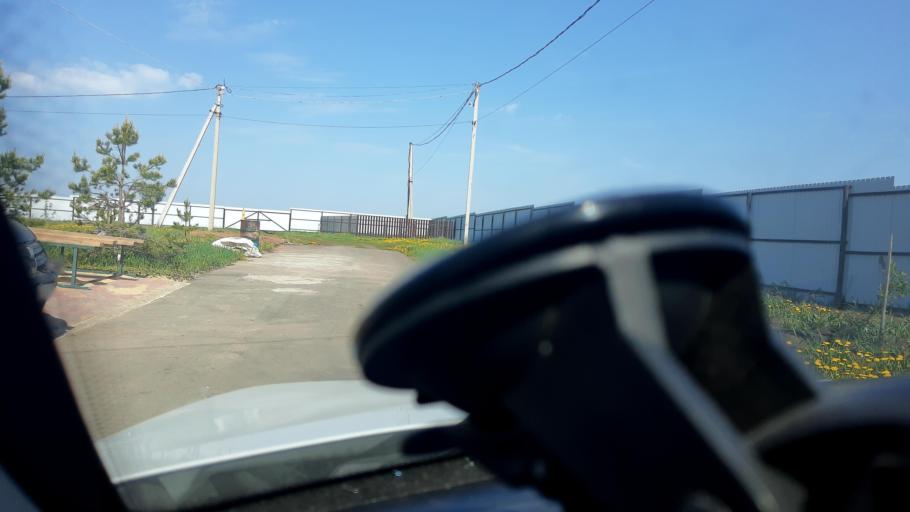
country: RU
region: Bashkortostan
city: Mikhaylovka
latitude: 54.7867
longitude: 55.7999
